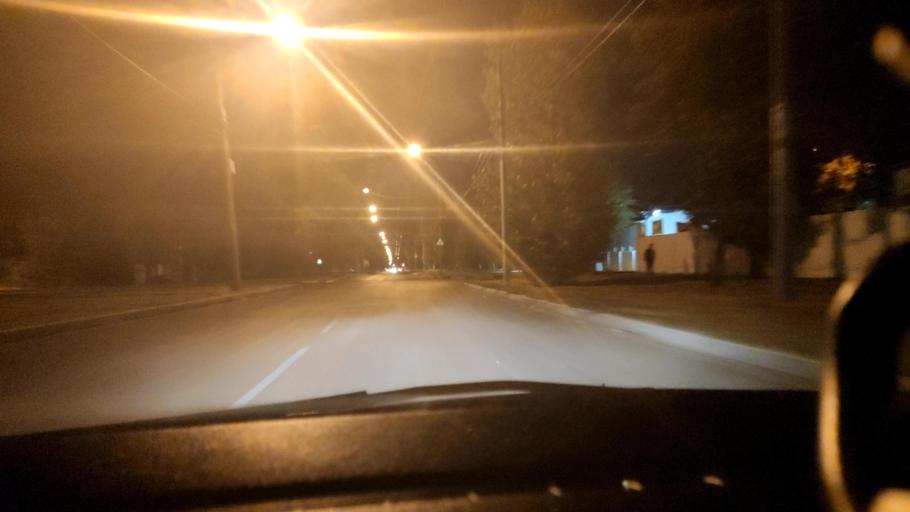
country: RU
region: Voronezj
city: Voronezh
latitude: 51.6375
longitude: 39.2452
